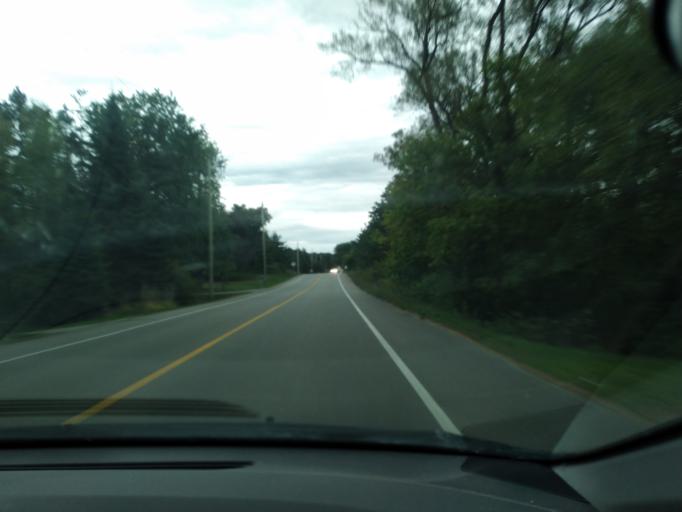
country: CA
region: Ontario
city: Bradford West Gwillimbury
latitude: 43.9753
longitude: -79.7982
